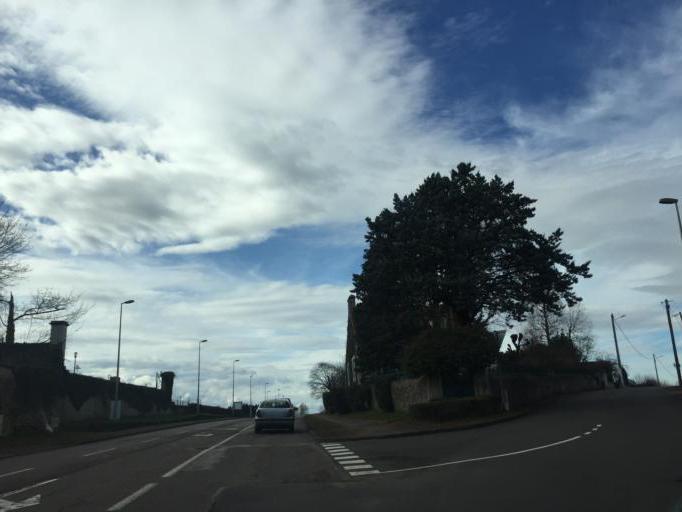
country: FR
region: Bourgogne
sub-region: Departement de l'Yonne
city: Avallon
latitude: 47.4949
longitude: 3.9026
